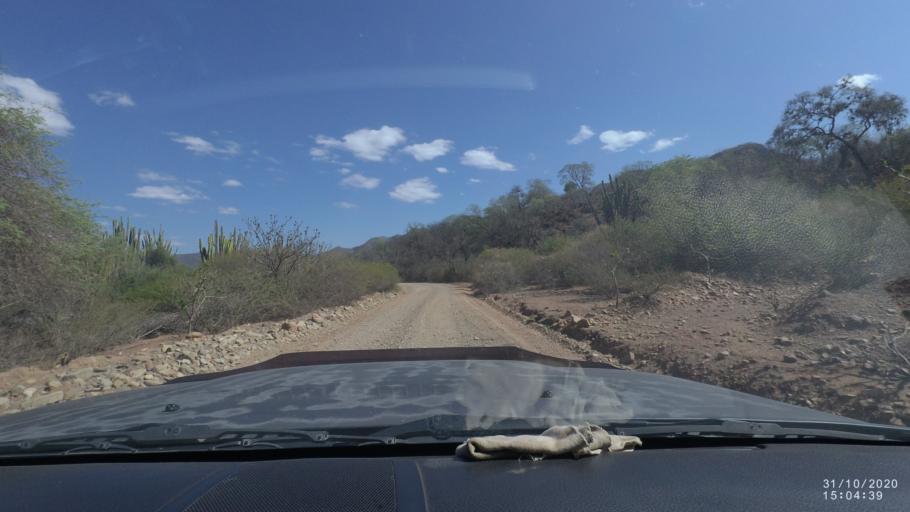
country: BO
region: Cochabamba
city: Aiquile
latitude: -18.2842
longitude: -64.8022
